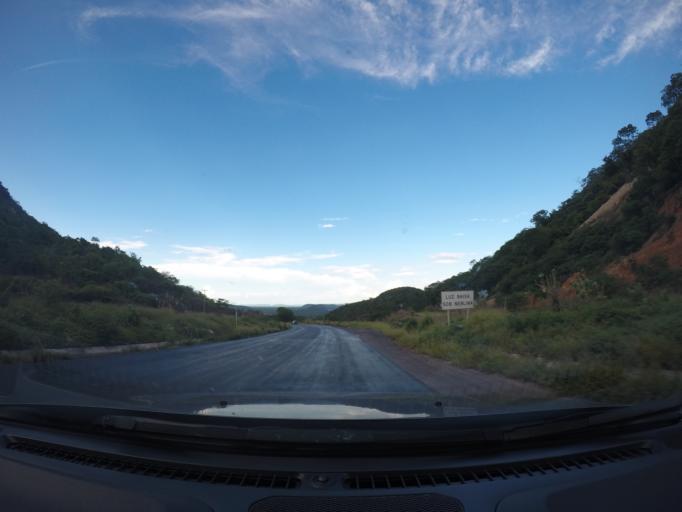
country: BR
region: Bahia
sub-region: Ibotirama
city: Ibotirama
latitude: -12.1401
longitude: -43.3520
